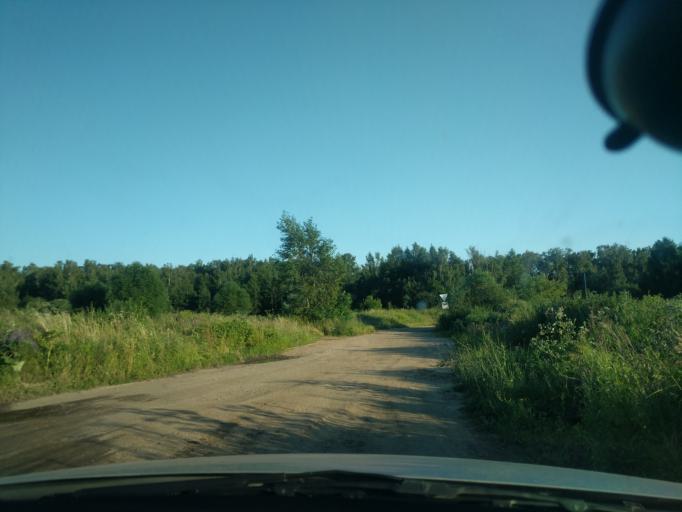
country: RU
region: Moskovskaya
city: Pushchino
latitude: 54.8440
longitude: 37.6408
